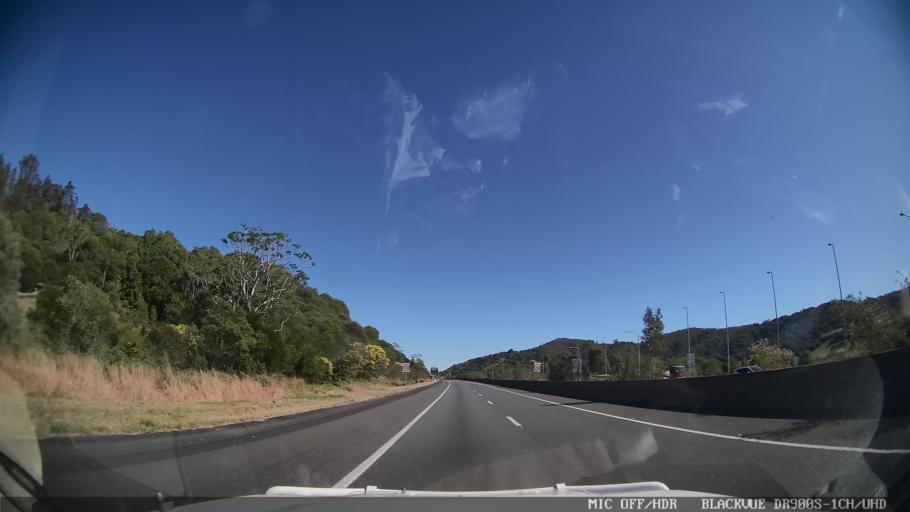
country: AU
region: Queensland
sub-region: Sunshine Coast
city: Black Mountain
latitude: -26.3901
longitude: 152.8060
